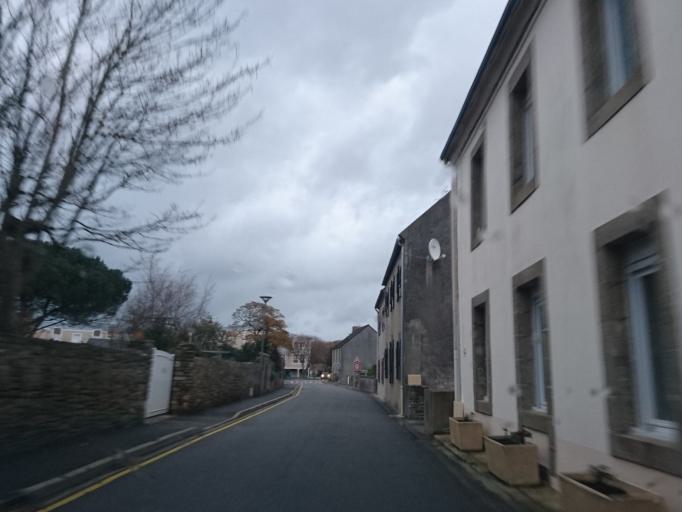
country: FR
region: Brittany
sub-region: Departement du Finistere
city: Le Conquet
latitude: 48.3582
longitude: -4.7718
